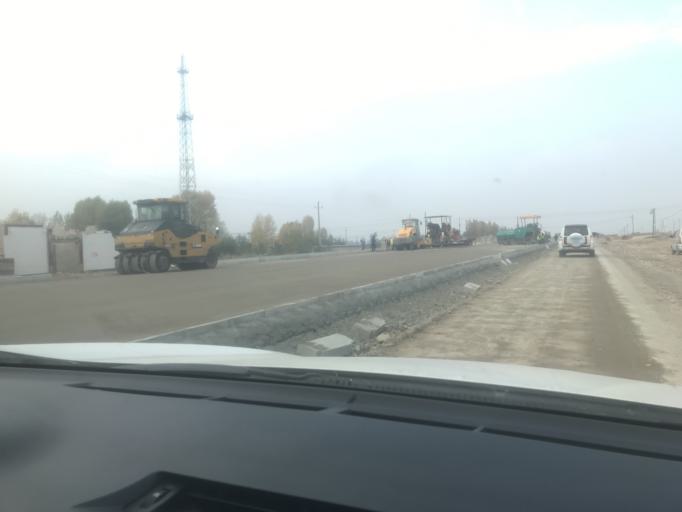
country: CN
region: Gansu Sheng
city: Gulang
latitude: 37.5159
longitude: 102.9008
